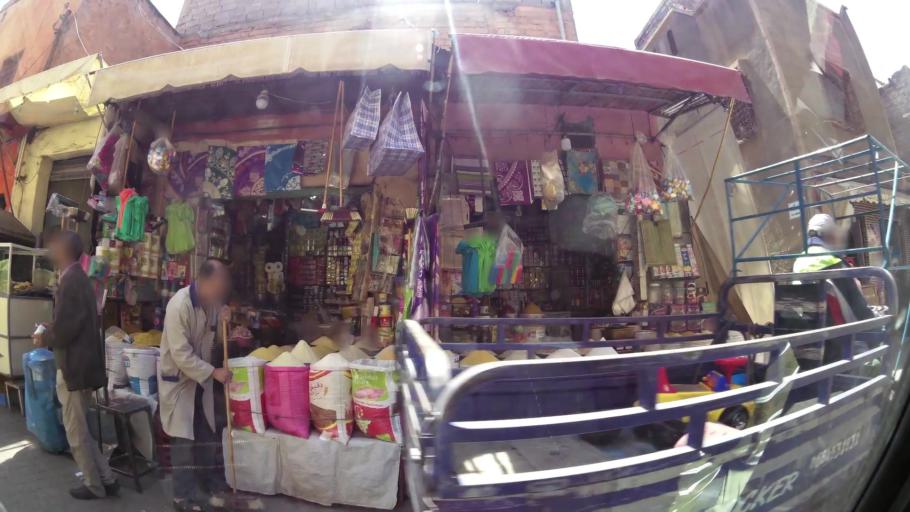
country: MA
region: Marrakech-Tensift-Al Haouz
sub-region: Marrakech
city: Marrakesh
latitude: 31.6179
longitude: -7.9690
